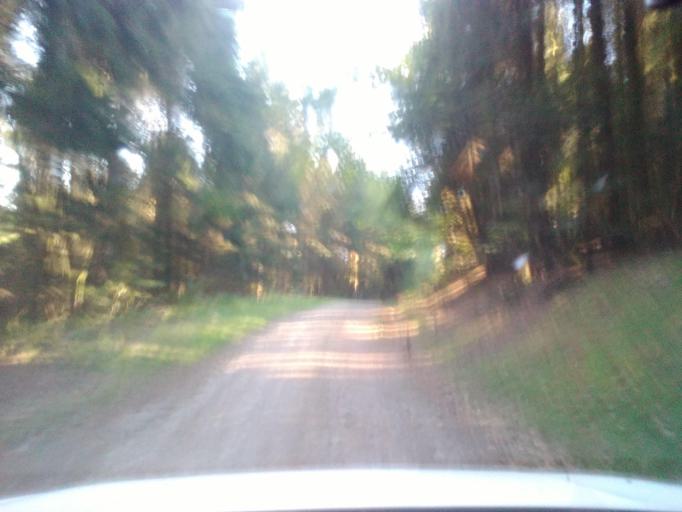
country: FR
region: Lorraine
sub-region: Departement des Vosges
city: Senones
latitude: 48.3450
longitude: 7.0631
